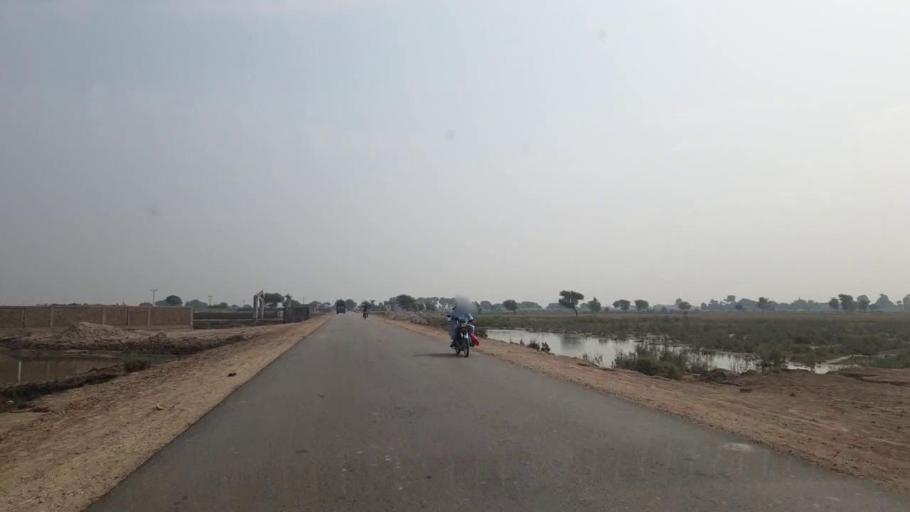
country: PK
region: Sindh
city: Matli
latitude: 25.0549
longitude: 68.6766
